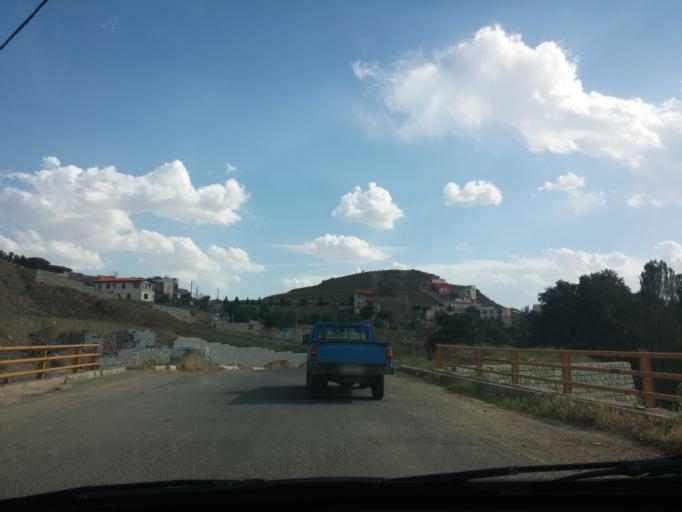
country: IR
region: Tehran
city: Damavand
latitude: 35.7295
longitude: 51.9061
